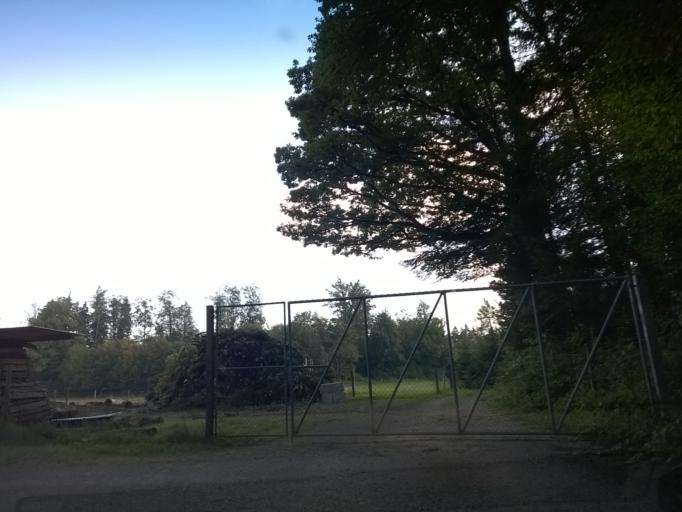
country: CH
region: Zurich
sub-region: Bezirk Buelach
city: Bachenbulach
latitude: 47.5003
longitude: 8.5653
